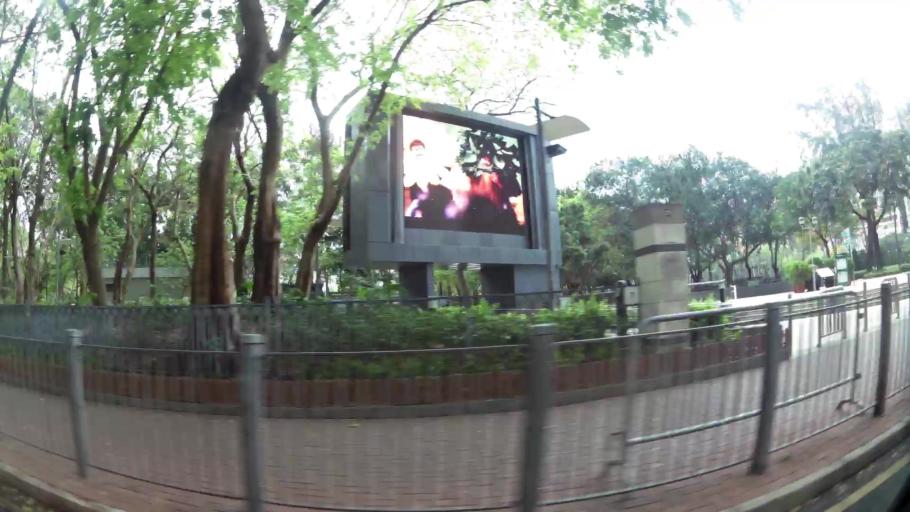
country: HK
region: Wanchai
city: Wan Chai
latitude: 22.2811
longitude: 114.1869
